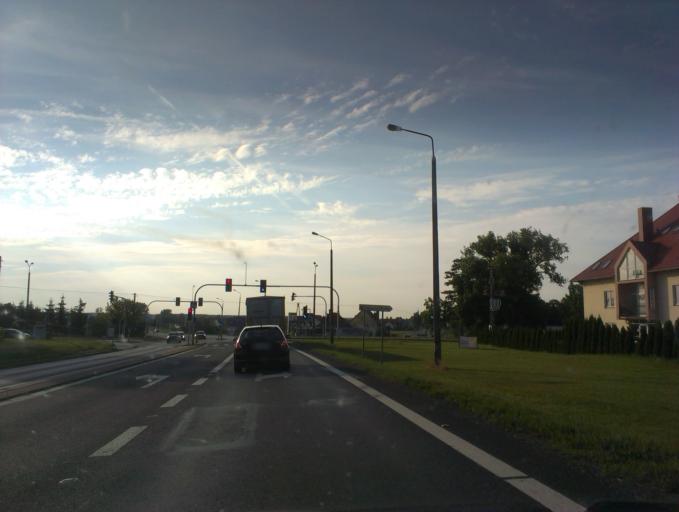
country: PL
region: Greater Poland Voivodeship
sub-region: Powiat leszczynski
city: Rydzyna
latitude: 51.7795
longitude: 16.6715
